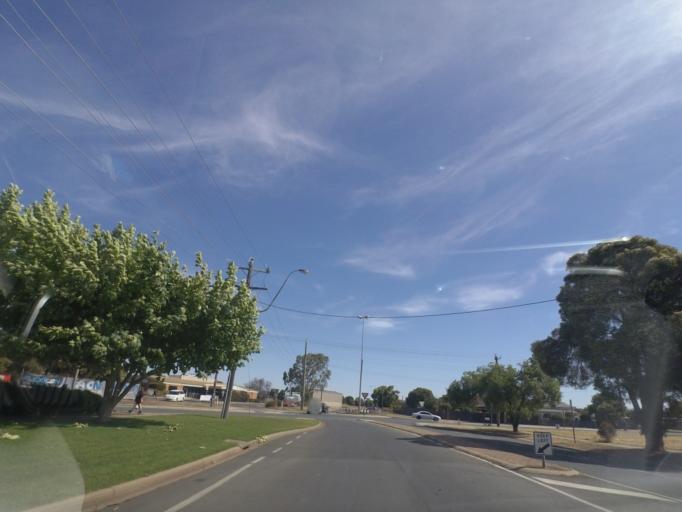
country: AU
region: Victoria
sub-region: Greater Shepparton
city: Shepparton
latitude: -36.3852
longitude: 145.4026
